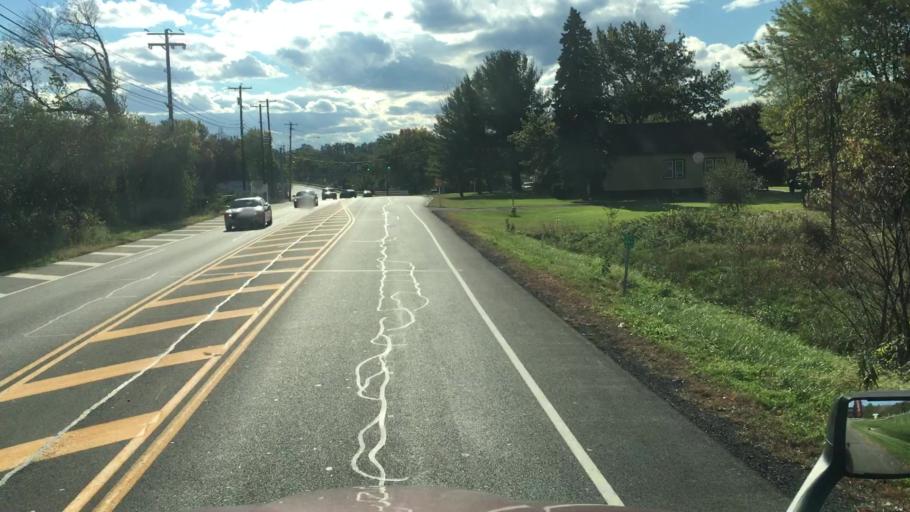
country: US
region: New York
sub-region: Schenectady County
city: Scotia
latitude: 42.8387
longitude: -73.9516
